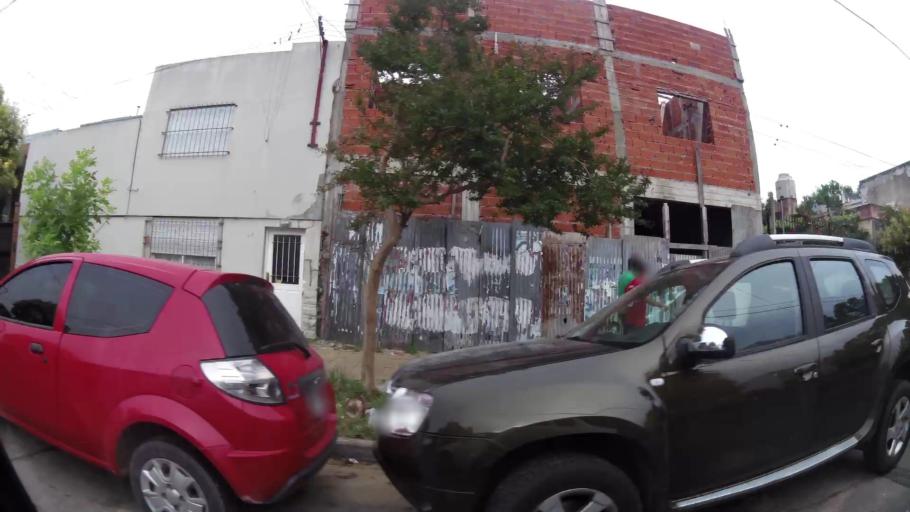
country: AR
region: Buenos Aires
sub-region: Partido de La Plata
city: La Plata
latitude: -34.9276
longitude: -57.9806
